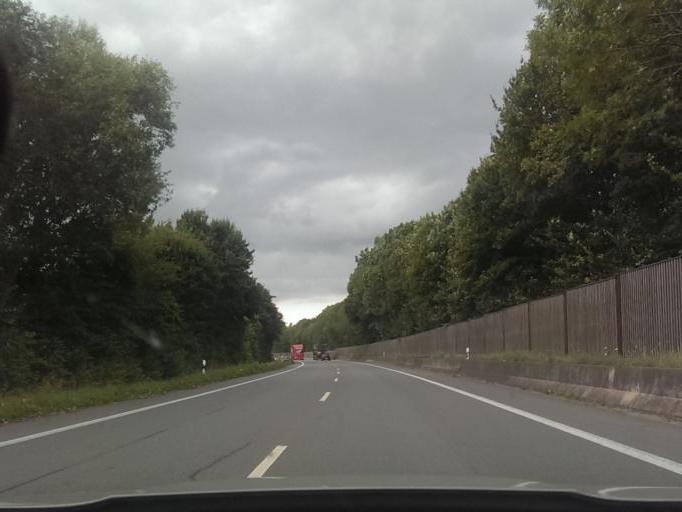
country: DE
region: North Rhine-Westphalia
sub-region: Regierungsbezirk Detmold
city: Steinheim
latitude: 51.8703
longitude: 9.1067
